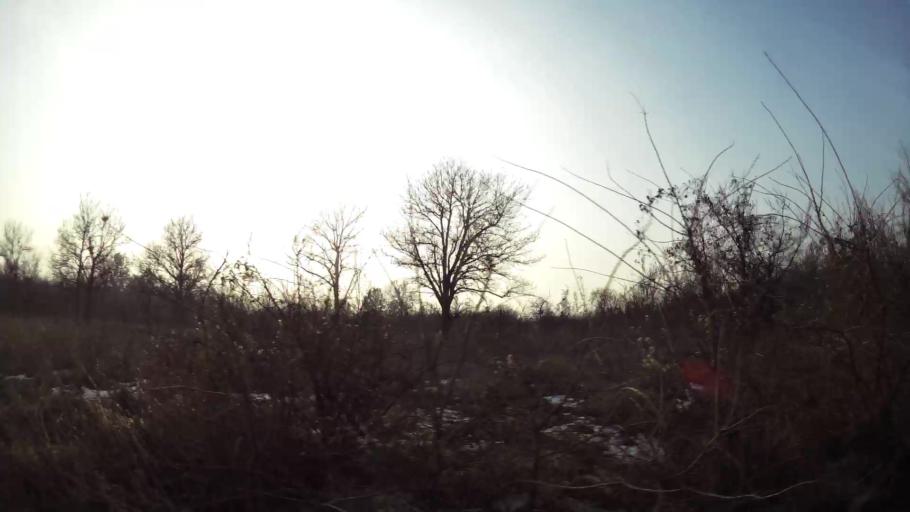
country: MK
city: Miladinovci
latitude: 41.9753
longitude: 21.6315
